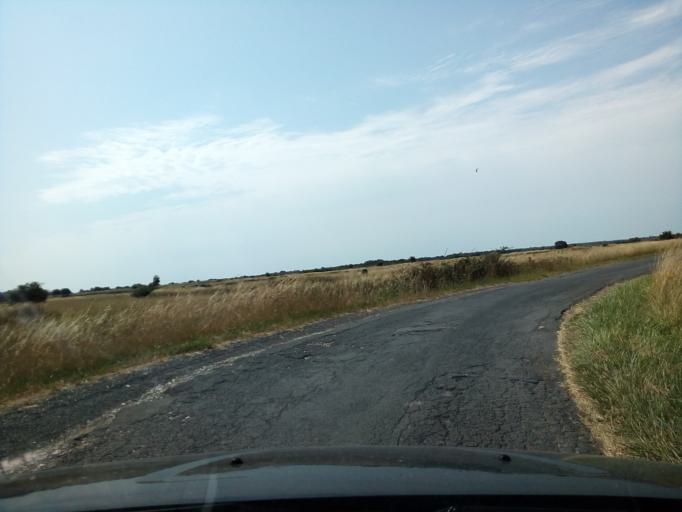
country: FR
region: Poitou-Charentes
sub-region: Departement de la Charente-Maritime
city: Boyard-Ville
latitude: 45.9538
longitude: -1.2632
